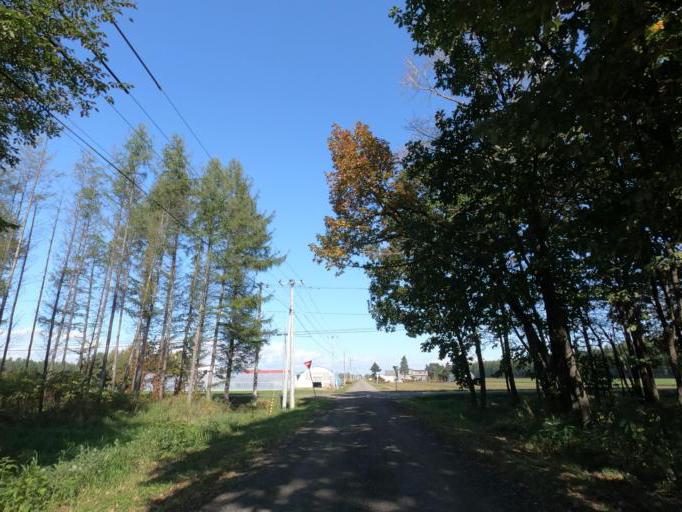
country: JP
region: Hokkaido
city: Otofuke
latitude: 43.0763
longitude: 143.2599
